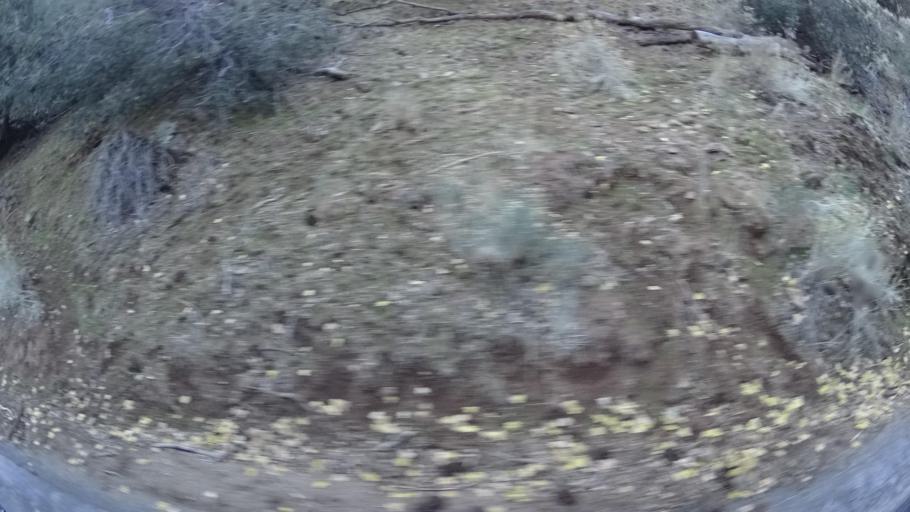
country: US
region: California
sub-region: Kern County
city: Golden Hills
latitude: 35.3006
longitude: -118.4693
